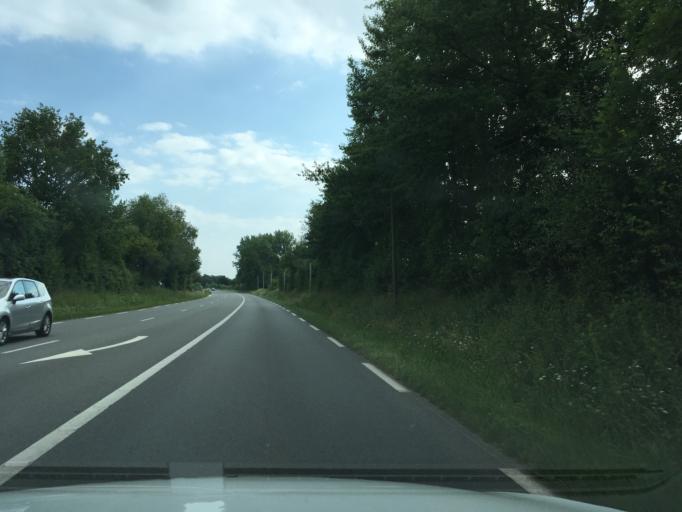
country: FR
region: Poitou-Charentes
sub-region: Departement des Deux-Sevres
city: Le Tallud
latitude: 46.6209
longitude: -0.2816
